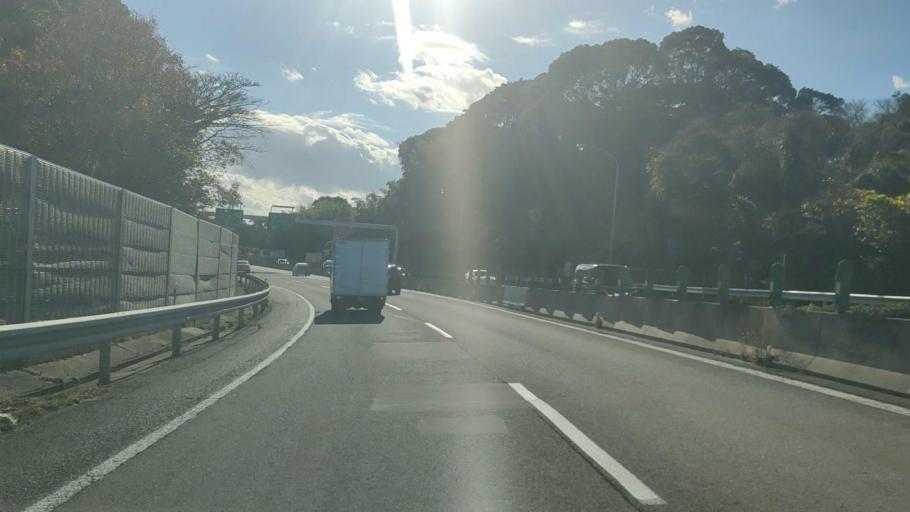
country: JP
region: Fukuoka
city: Kitakyushu
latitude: 33.8493
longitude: 130.7674
